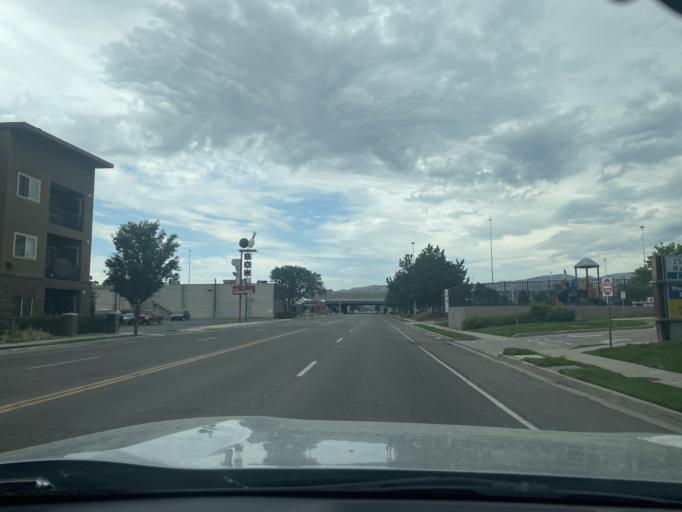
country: US
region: Utah
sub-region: Salt Lake County
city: South Salt Lake
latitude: 40.7155
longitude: -111.8911
